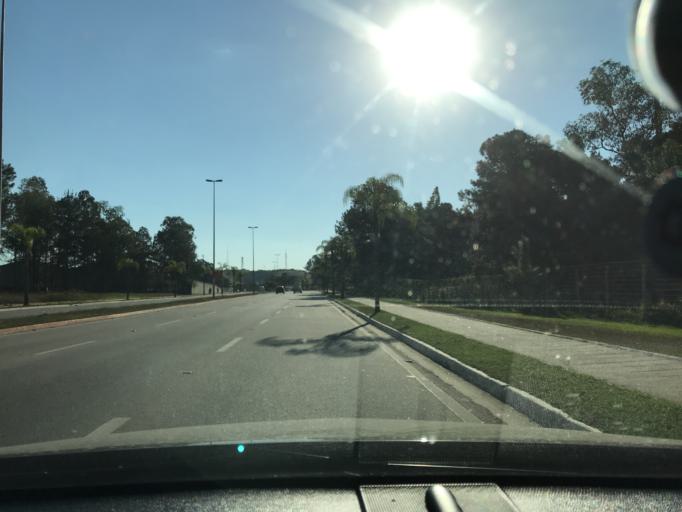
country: BR
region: Sao Paulo
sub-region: Sao Jose Dos Campos
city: Sao Jose dos Campos
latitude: -23.1659
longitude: -45.8971
